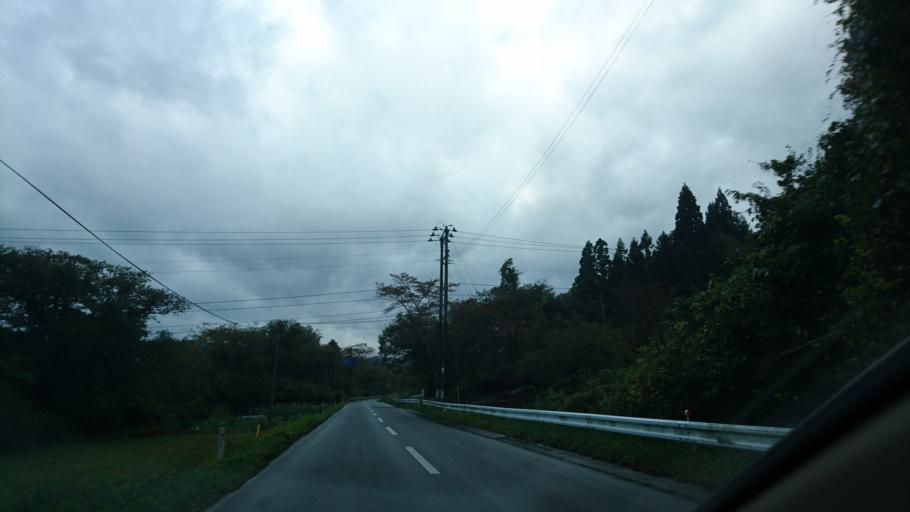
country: JP
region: Iwate
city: Ichinoseki
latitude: 38.9493
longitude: 141.0297
